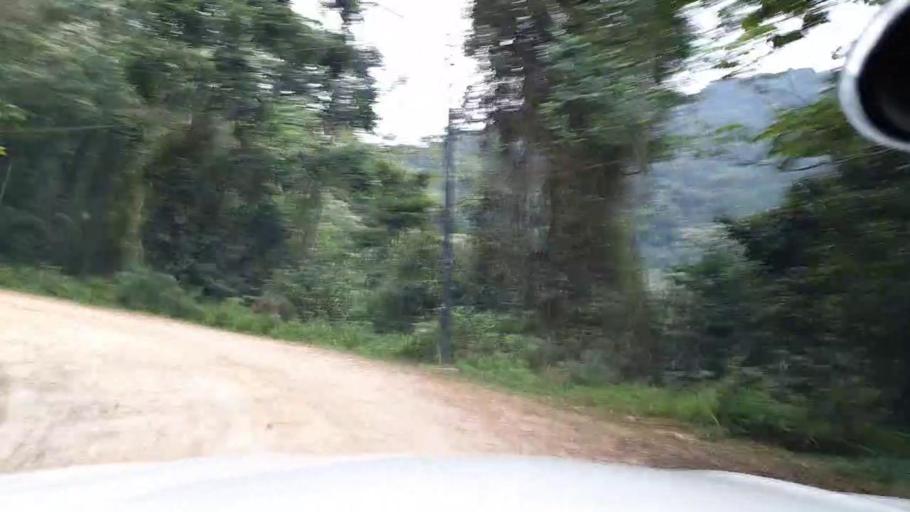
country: BI
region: Cibitoke
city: Cibitoke
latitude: -2.5707
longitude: 29.2292
